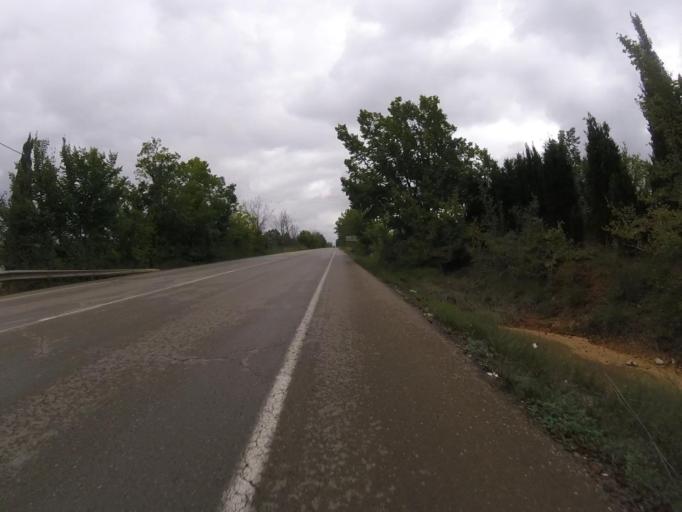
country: ES
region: Valencia
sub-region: Provincia de Castello
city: Cabanes
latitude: 40.1598
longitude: 0.0416
